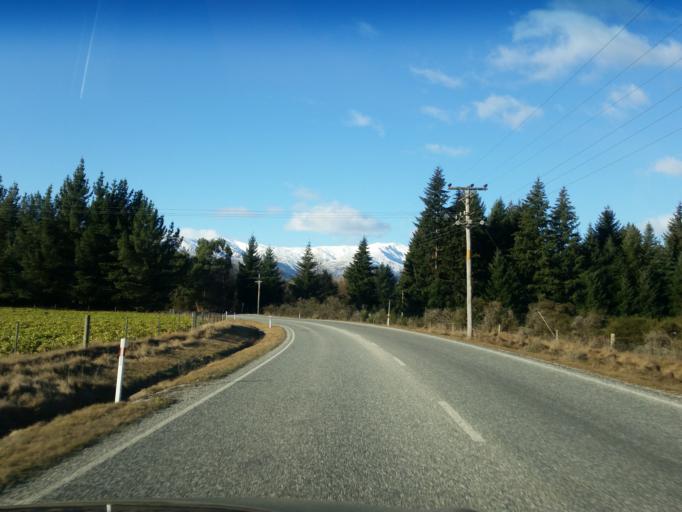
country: NZ
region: Otago
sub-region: Queenstown-Lakes District
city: Arrowtown
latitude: -44.9558
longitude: 168.7401
